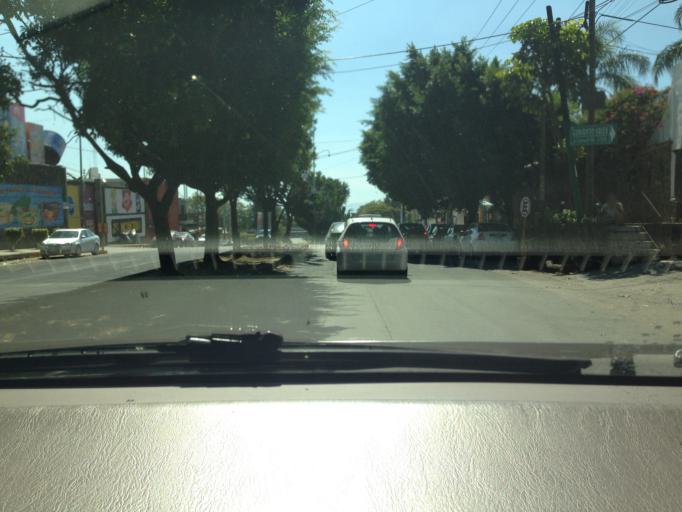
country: MX
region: Morelos
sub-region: Cuernavaca
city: Fraccionamiento Lomas de Ahuatlan
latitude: 18.9629
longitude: -99.2283
